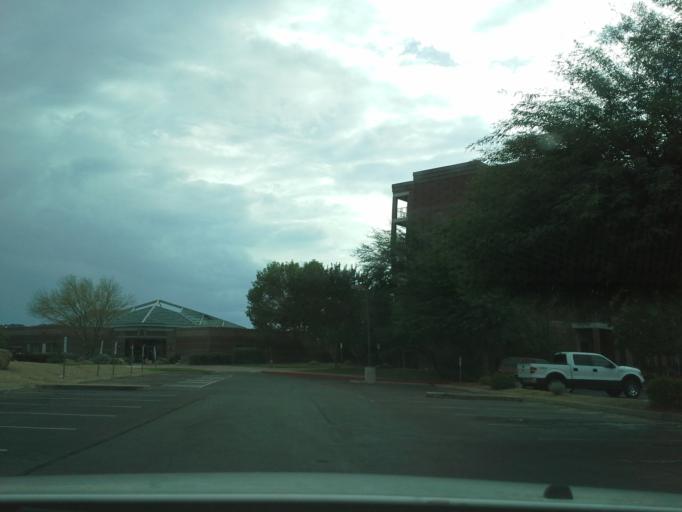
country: US
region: Arizona
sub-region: Maricopa County
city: Paradise Valley
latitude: 33.5961
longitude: -111.9846
